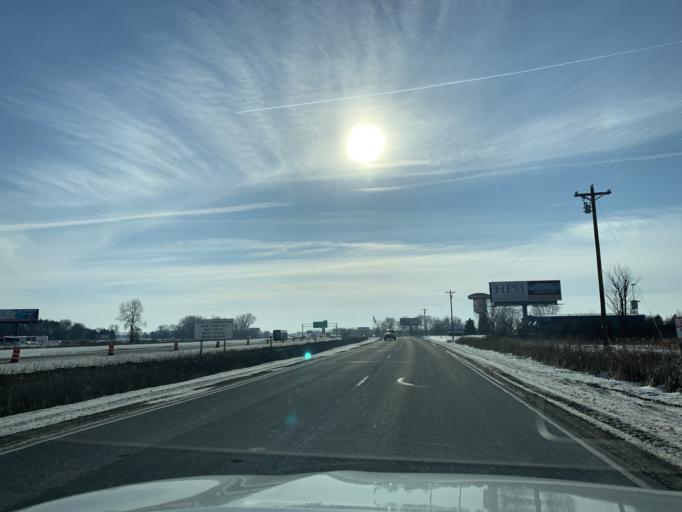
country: US
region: Minnesota
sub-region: Anoka County
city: Columbus
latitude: 45.2454
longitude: -93.0278
